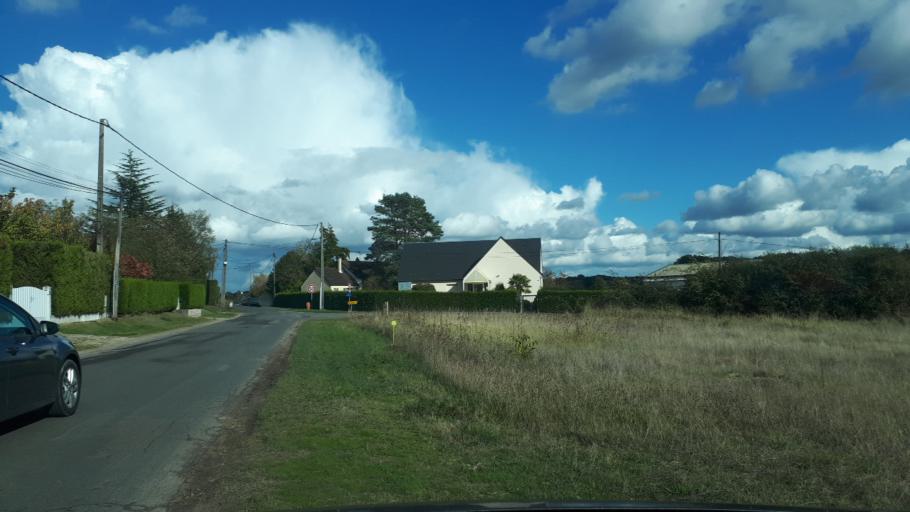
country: FR
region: Centre
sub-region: Departement du Loir-et-Cher
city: Thesee
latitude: 47.3222
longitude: 1.3187
